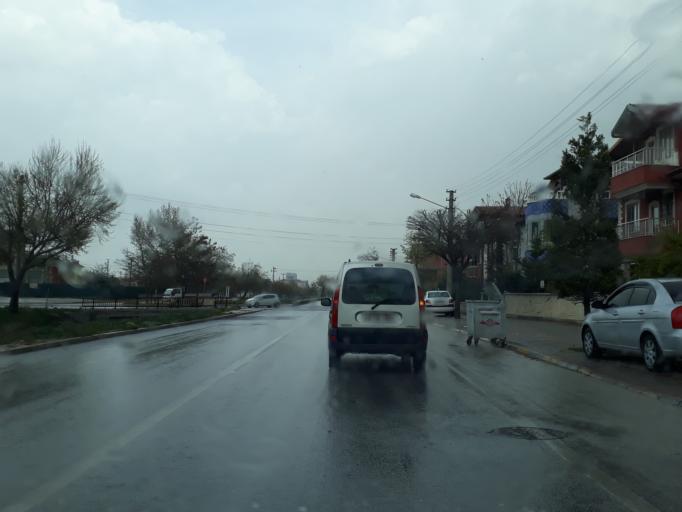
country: TR
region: Konya
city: Selcuklu
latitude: 37.9201
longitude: 32.4859
